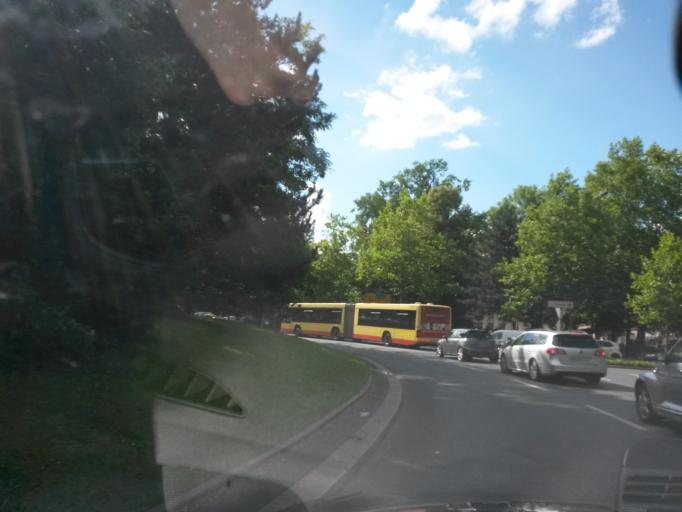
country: DE
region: Bavaria
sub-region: Regierungsbezirk Unterfranken
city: Wuerzburg
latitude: 49.7987
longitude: 9.9432
